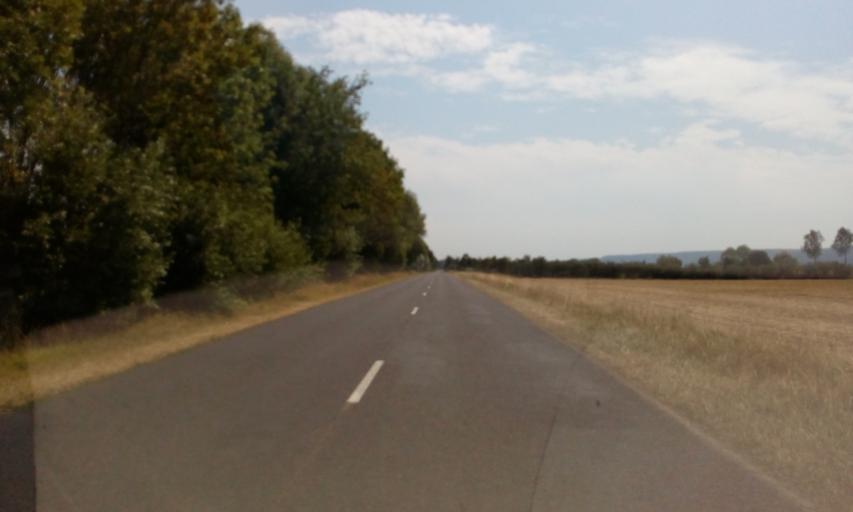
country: FR
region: Lorraine
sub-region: Departement de la Meuse
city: Vigneulles-les-Hattonchatel
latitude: 49.0829
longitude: 5.6353
